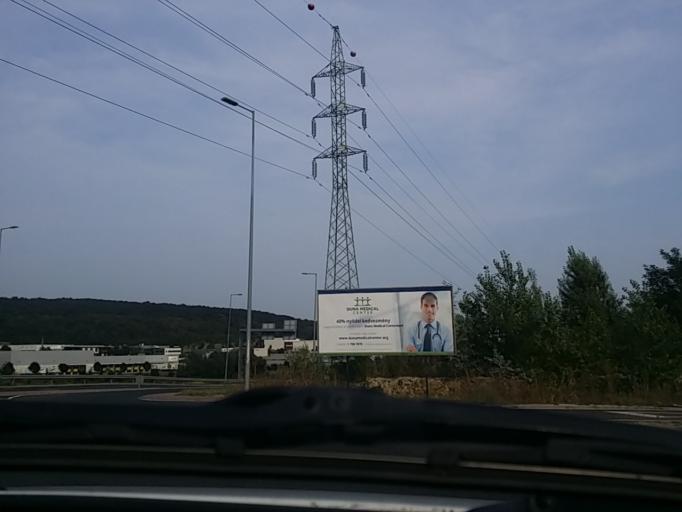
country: HU
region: Pest
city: Biatorbagy
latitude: 47.4723
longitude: 18.8650
